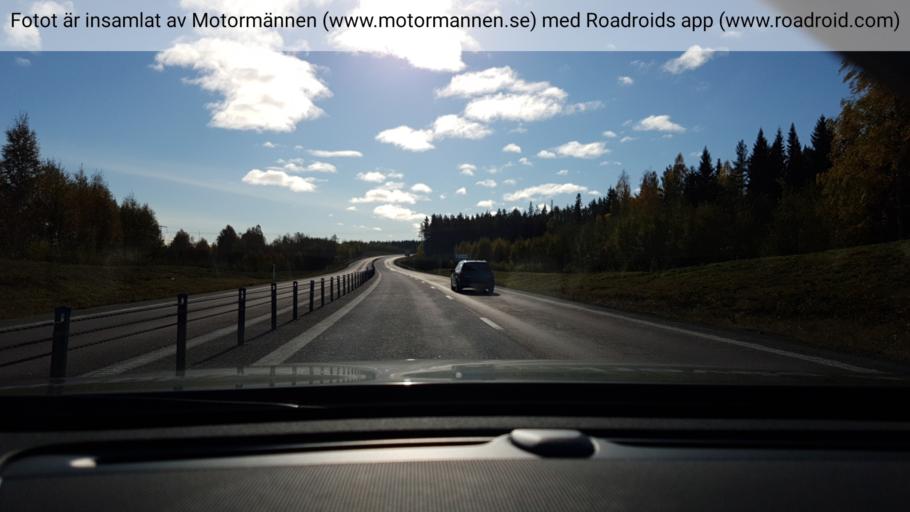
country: SE
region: Vaesterbotten
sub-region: Skelleftea Kommun
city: Skelleftea
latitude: 64.7198
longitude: 20.9870
